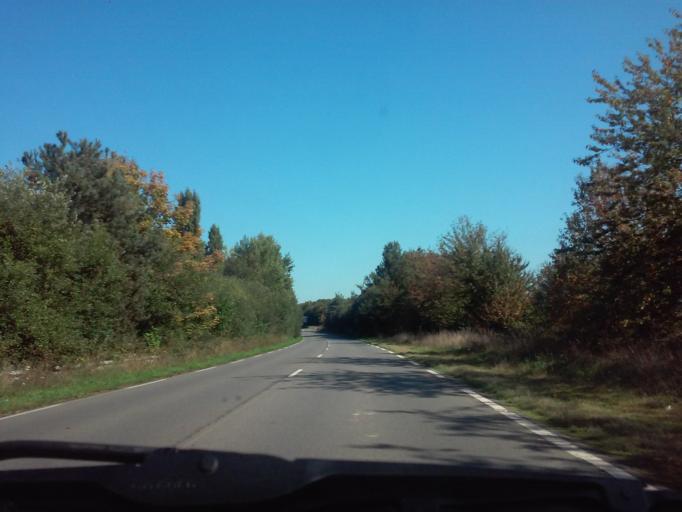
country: FR
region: Brittany
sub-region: Departement d'Ille-et-Vilaine
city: Betton
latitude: 48.1544
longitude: -1.6521
